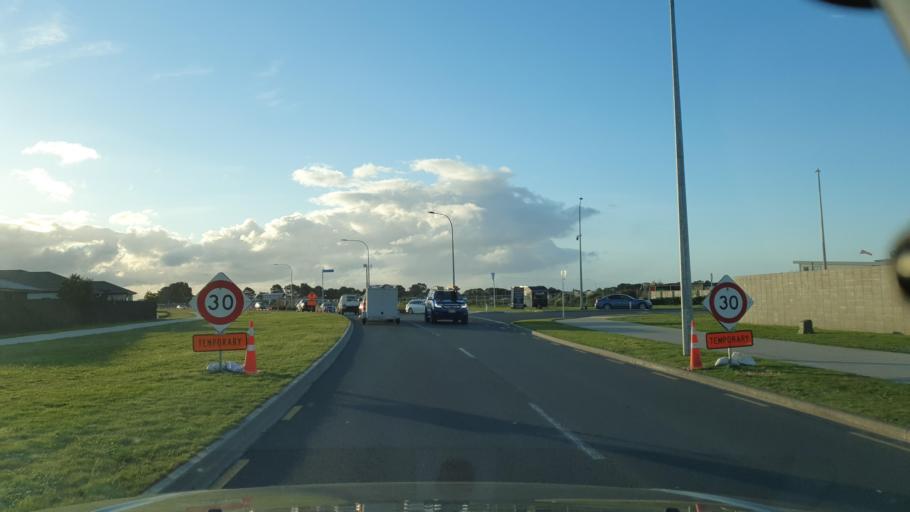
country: NZ
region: Bay of Plenty
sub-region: Western Bay of Plenty District
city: Maketu
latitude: -37.7159
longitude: 176.3140
